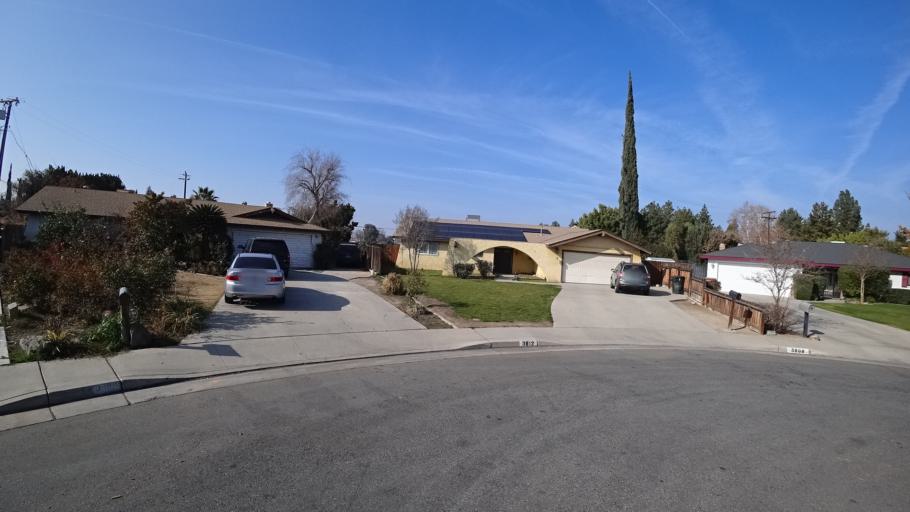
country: US
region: California
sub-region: Kern County
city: Bakersfield
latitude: 35.3209
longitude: -119.0451
